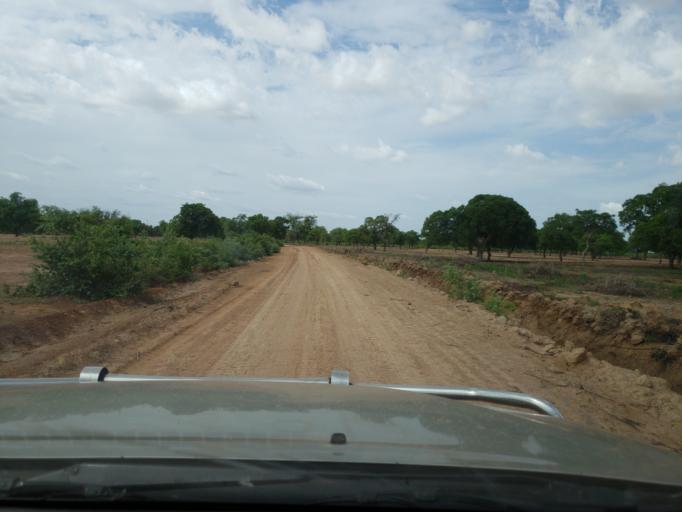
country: ML
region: Segou
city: Bla
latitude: 12.7152
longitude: -5.6842
